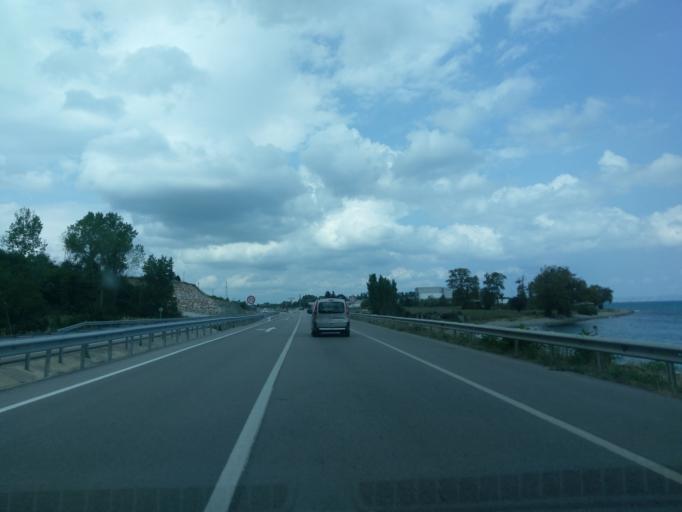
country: TR
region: Sinop
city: Gerze
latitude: 41.8312
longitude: 35.1595
